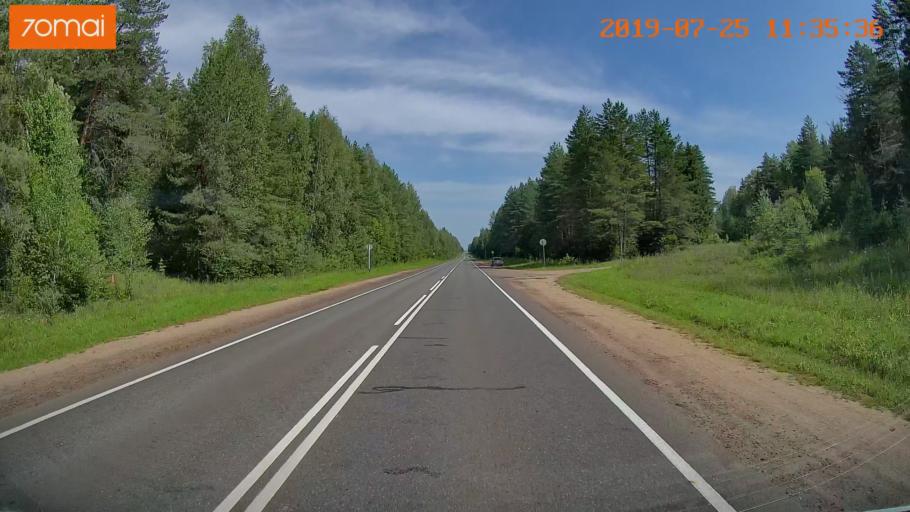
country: RU
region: Ivanovo
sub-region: Privolzhskiy Rayon
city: Ples
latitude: 57.4139
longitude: 41.4321
